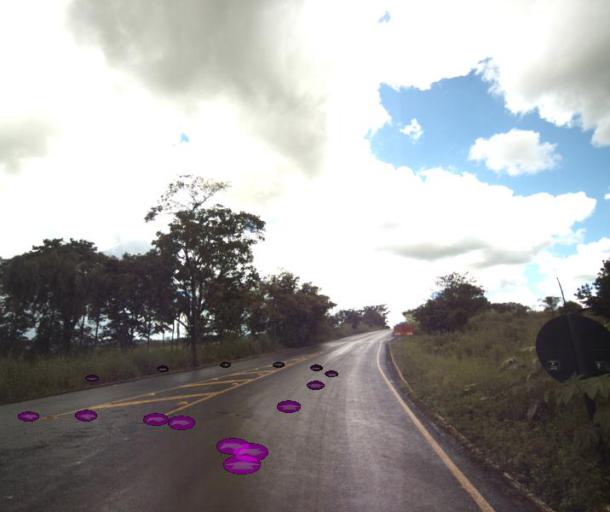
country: BR
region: Goias
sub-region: Pirenopolis
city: Pirenopolis
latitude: -16.0477
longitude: -49.0739
